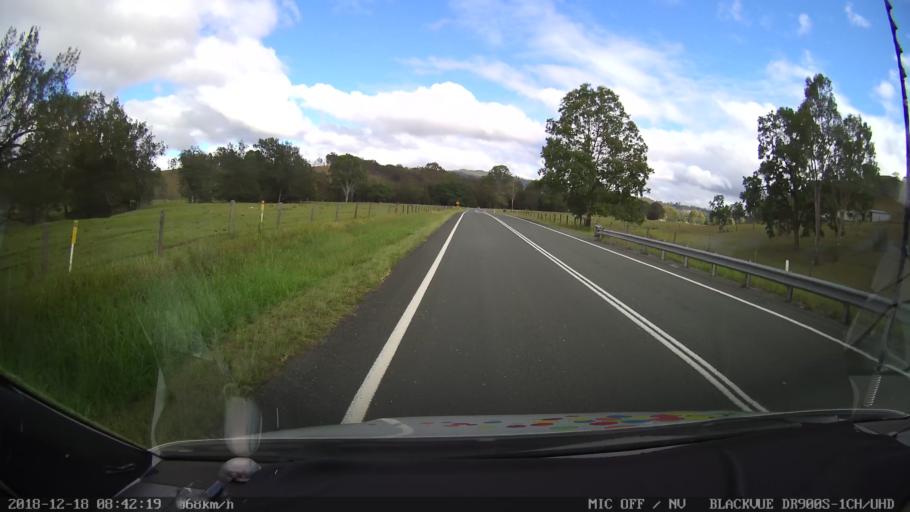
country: AU
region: Queensland
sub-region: Logan
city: Cedar Vale
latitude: -28.2280
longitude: 152.8599
